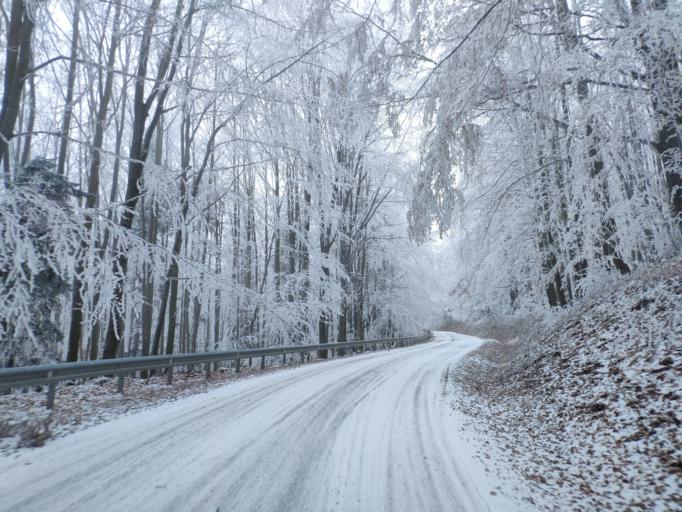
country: SK
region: Kosicky
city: Dobsina
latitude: 48.8067
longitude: 20.4840
